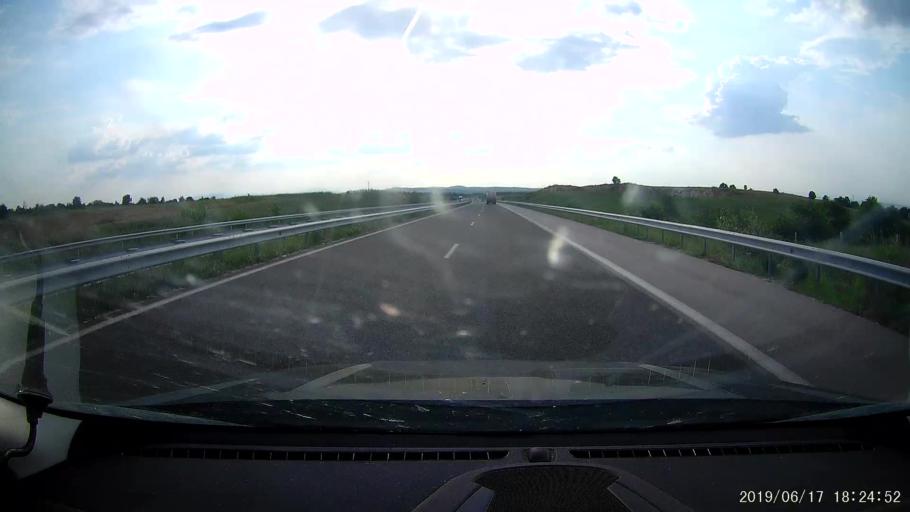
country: BG
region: Khaskovo
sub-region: Obshtina Dimitrovgrad
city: Dimitrovgrad
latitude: 41.9881
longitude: 25.6785
